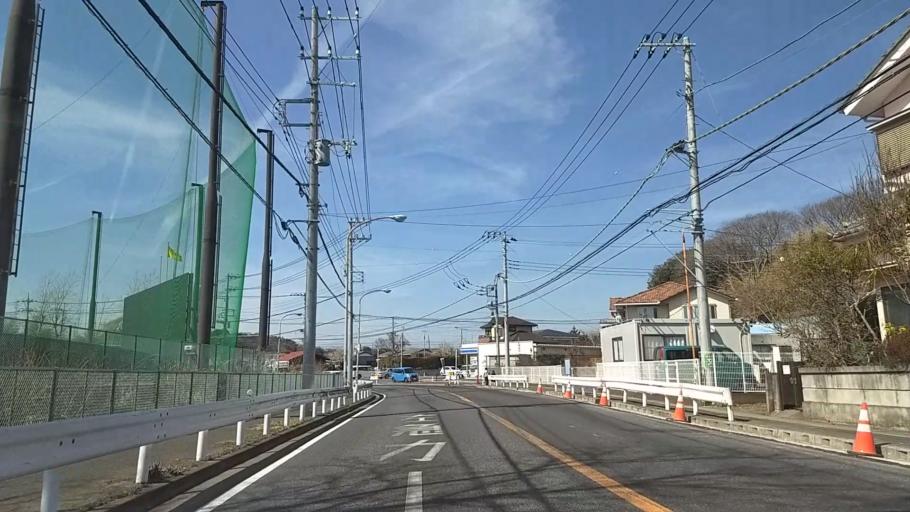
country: JP
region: Kanagawa
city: Fujisawa
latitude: 35.3814
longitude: 139.4927
